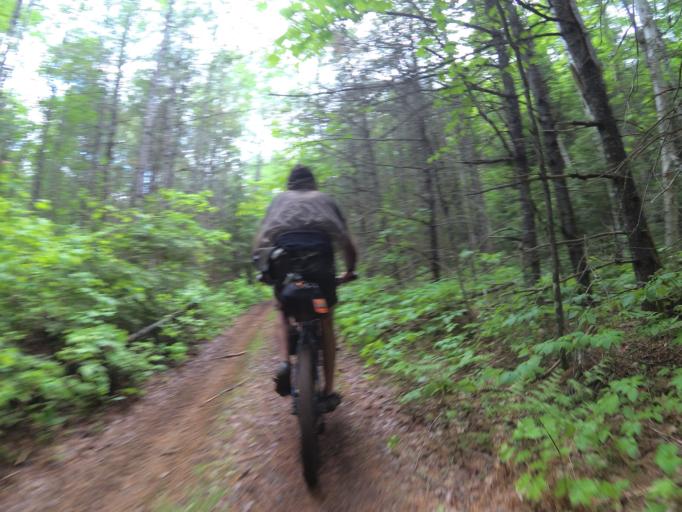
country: CA
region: Ontario
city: Renfrew
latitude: 45.1150
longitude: -76.8527
